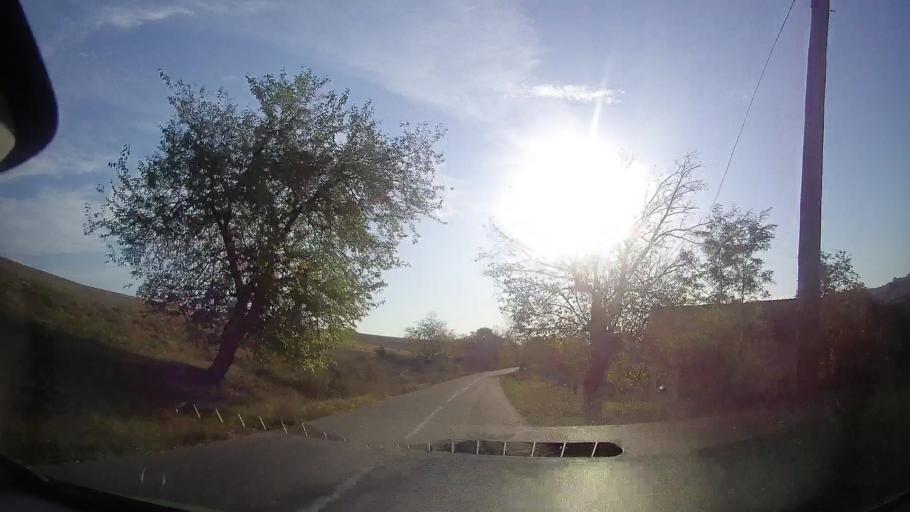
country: RO
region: Timis
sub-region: Comuna Bogda
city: Bogda
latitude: 45.9769
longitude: 21.5833
